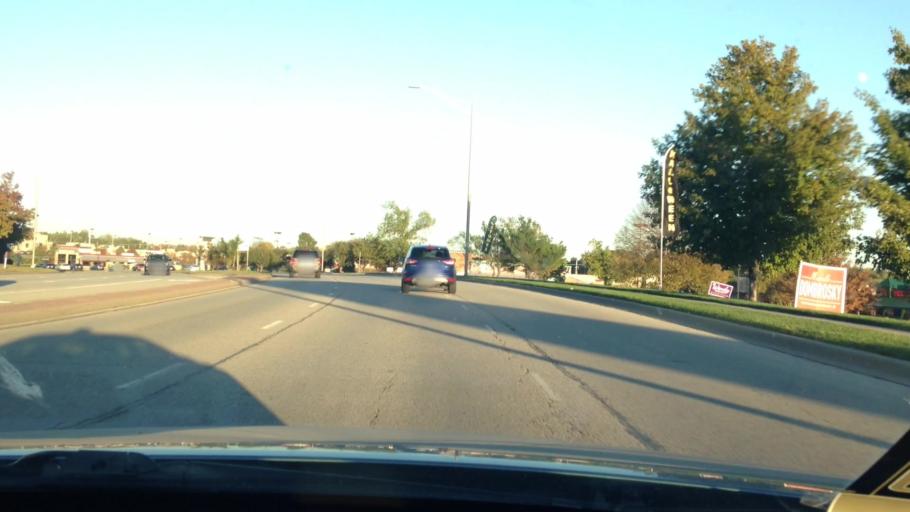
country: US
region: Kansas
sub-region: Johnson County
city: Lenexa
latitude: 38.9100
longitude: -94.7698
